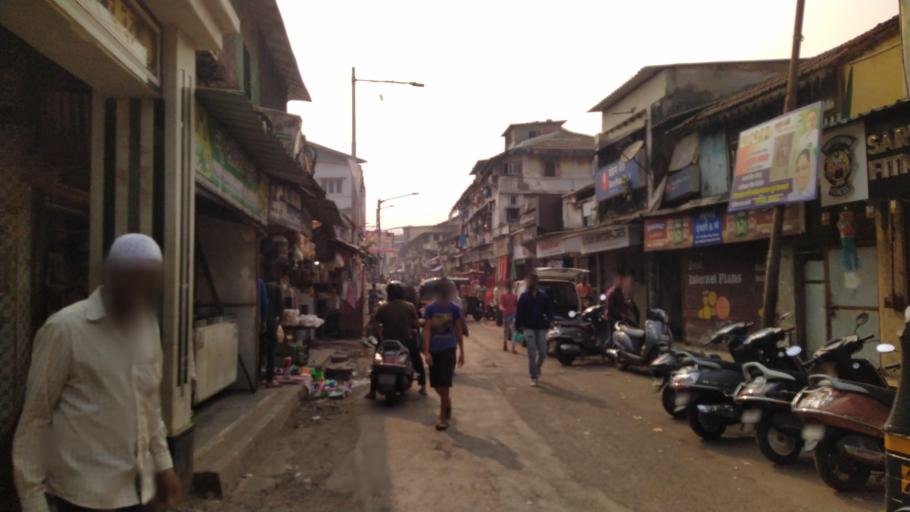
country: IN
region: Maharashtra
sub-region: Mumbai Suburban
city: Mumbai
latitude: 19.0645
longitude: 72.8762
